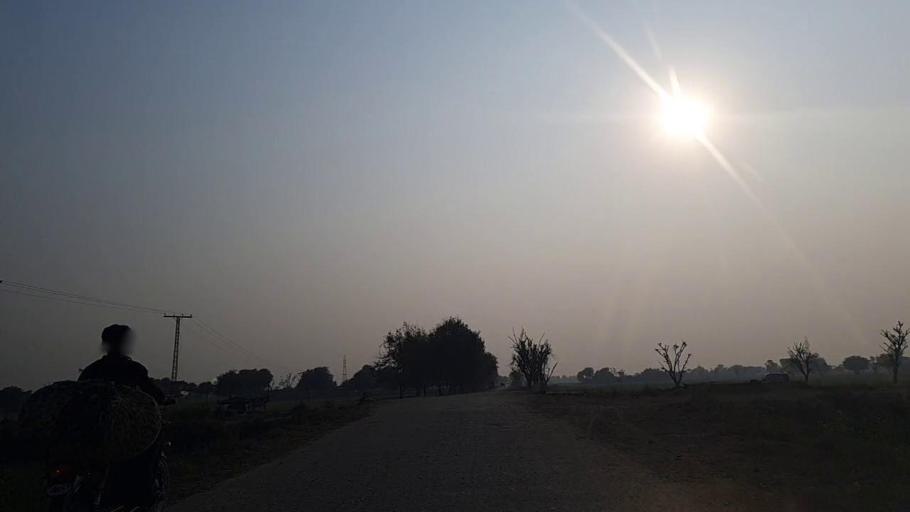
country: PK
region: Sindh
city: Nawabshah
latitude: 26.2296
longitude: 68.4840
